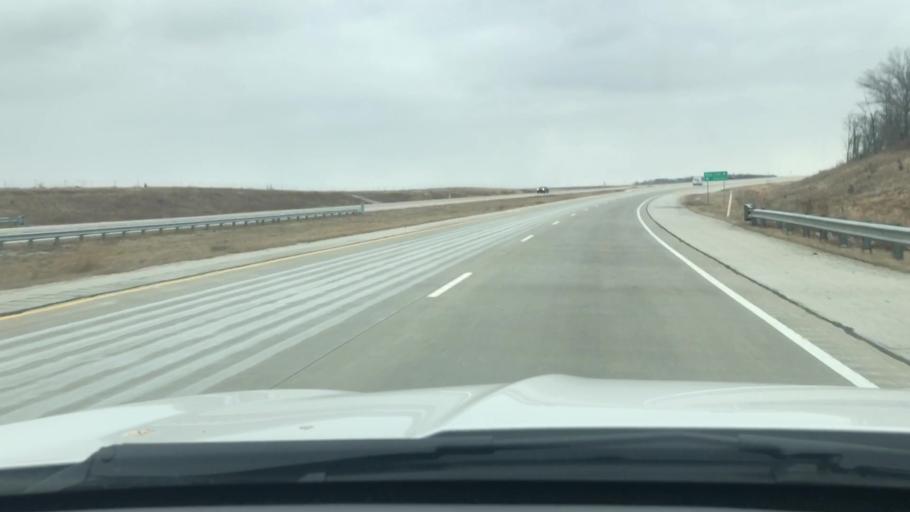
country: US
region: Indiana
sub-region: Tippecanoe County
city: Battle Ground
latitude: 40.4907
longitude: -86.7669
